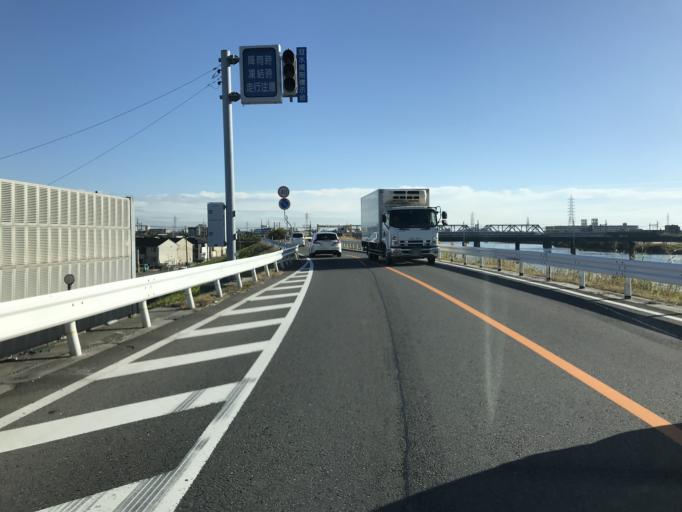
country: JP
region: Aichi
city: Kanie
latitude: 35.1464
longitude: 136.8317
